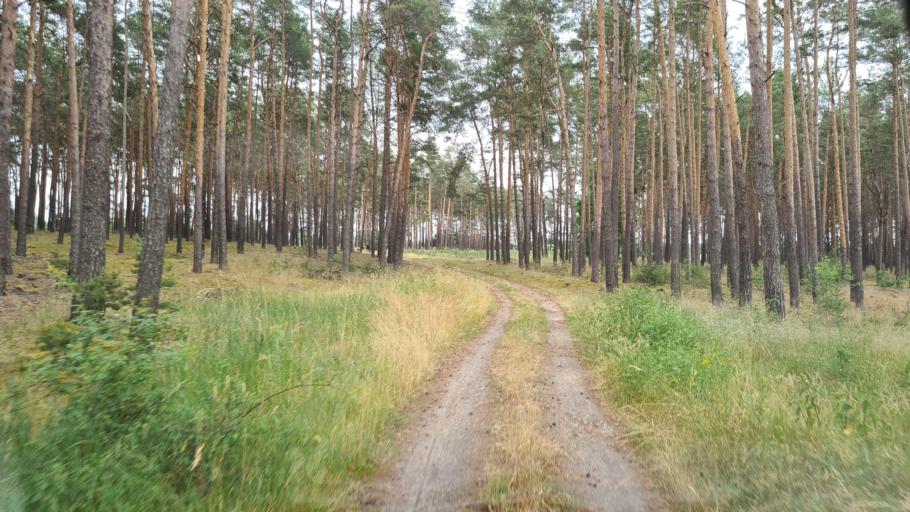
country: DE
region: Brandenburg
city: Schilda
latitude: 51.6474
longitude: 13.3804
